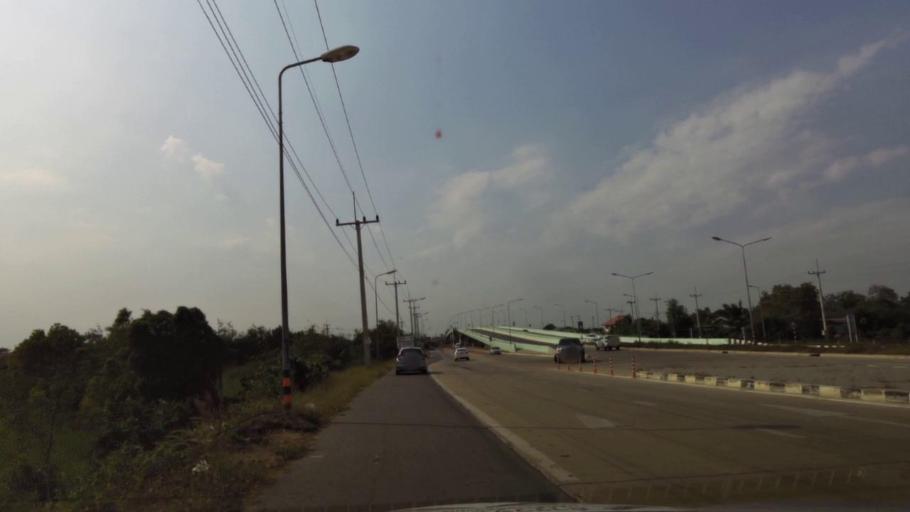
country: TH
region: Phra Nakhon Si Ayutthaya
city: Phra Nakhon Si Ayutthaya
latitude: 14.3288
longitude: 100.5801
